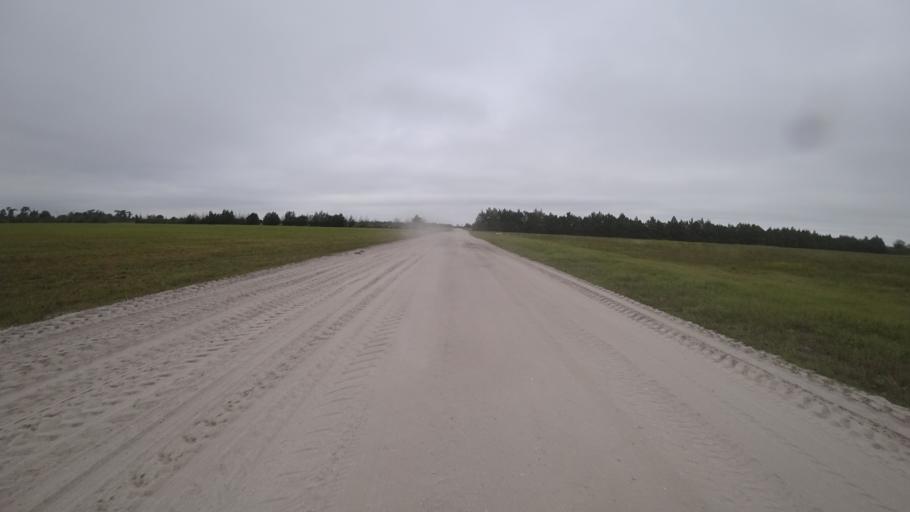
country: US
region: Florida
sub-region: Sarasota County
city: Warm Mineral Springs
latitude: 27.2998
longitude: -82.1280
